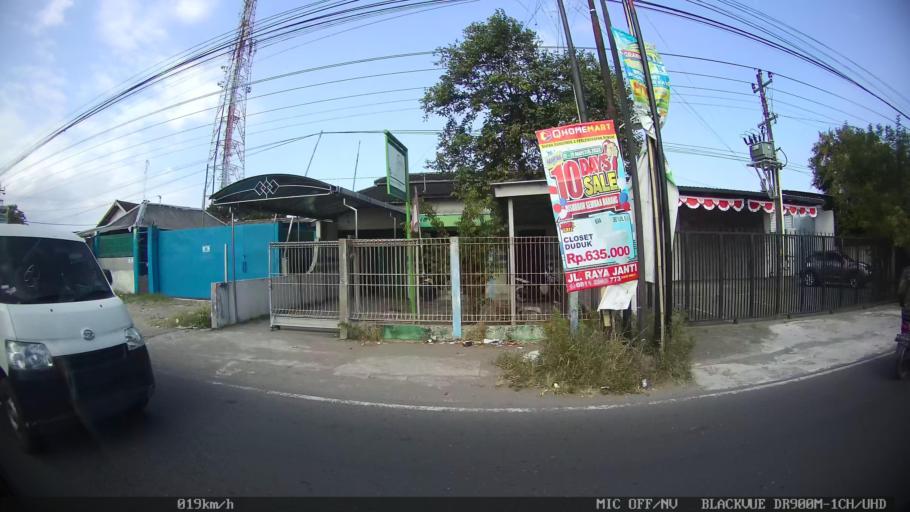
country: ID
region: Daerah Istimewa Yogyakarta
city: Sewon
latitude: -7.8533
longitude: 110.3902
